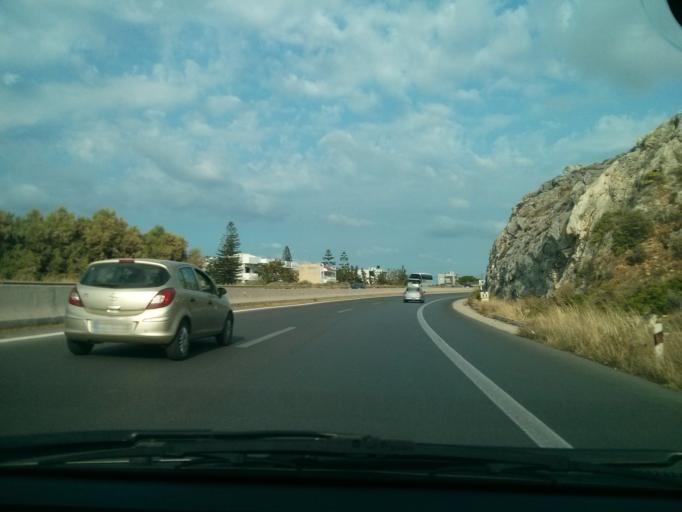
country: GR
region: Crete
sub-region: Nomos Irakleiou
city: Kokkini Hani
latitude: 35.3302
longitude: 25.2420
